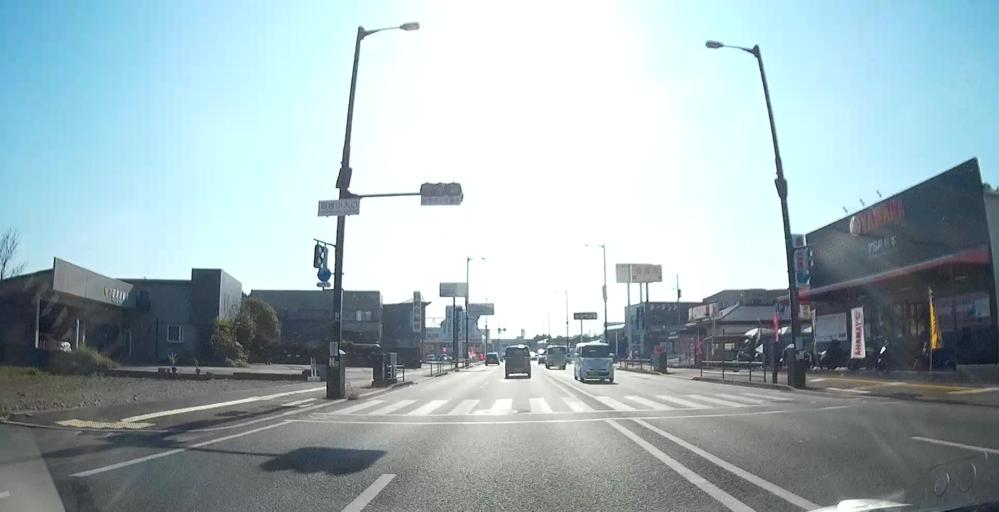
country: JP
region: Kumamoto
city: Kumamoto
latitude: 32.7656
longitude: 130.6910
